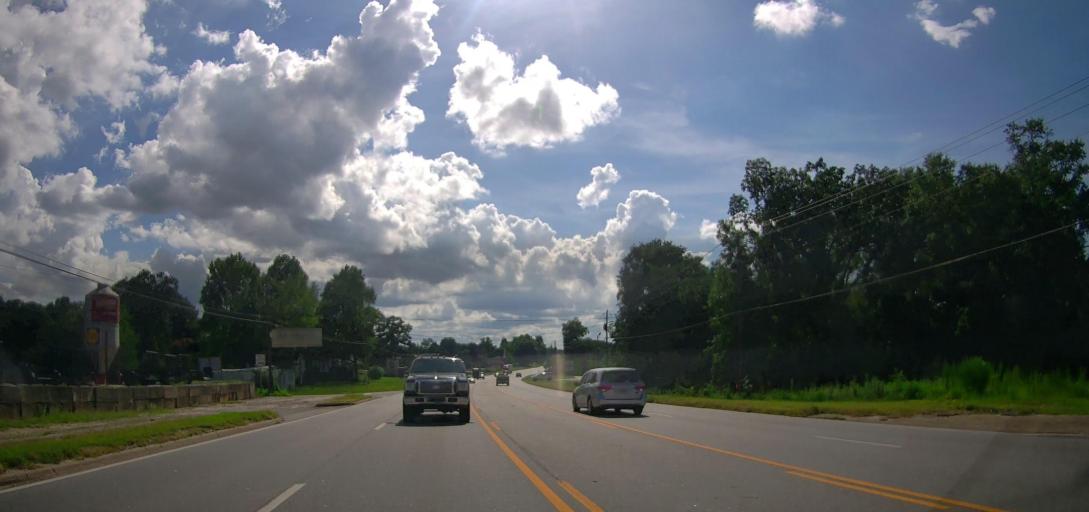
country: US
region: Alabama
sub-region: Russell County
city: Ladonia
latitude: 32.4682
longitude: -85.0683
